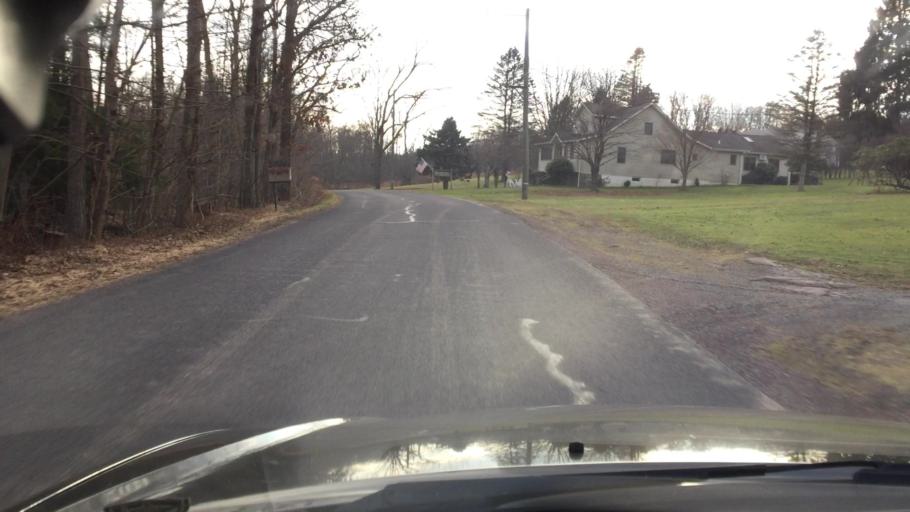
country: US
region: Pennsylvania
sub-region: Luzerne County
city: Back Mountain
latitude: 41.2934
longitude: -76.0478
